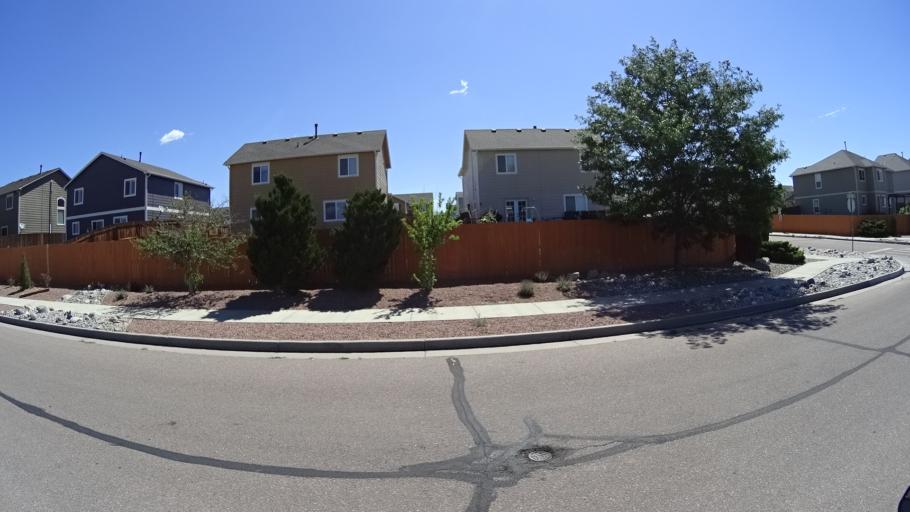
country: US
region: Colorado
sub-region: El Paso County
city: Security-Widefield
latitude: 38.7772
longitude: -104.6576
